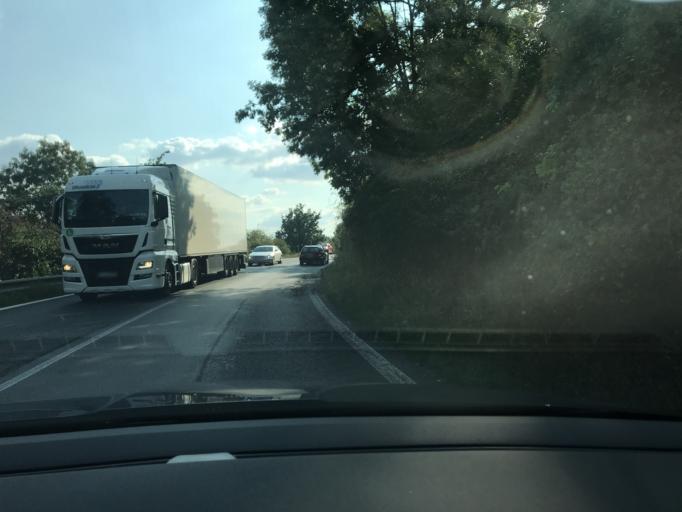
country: CZ
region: Central Bohemia
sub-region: Okres Kladno
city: Slany
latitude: 50.2423
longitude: 14.1370
